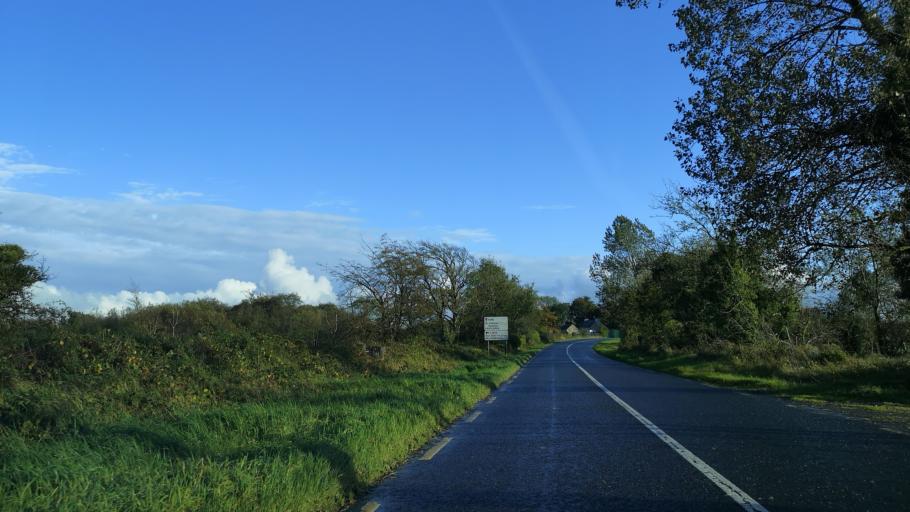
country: IE
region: Connaught
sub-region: Roscommon
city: Castlerea
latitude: 53.7842
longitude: -8.4871
